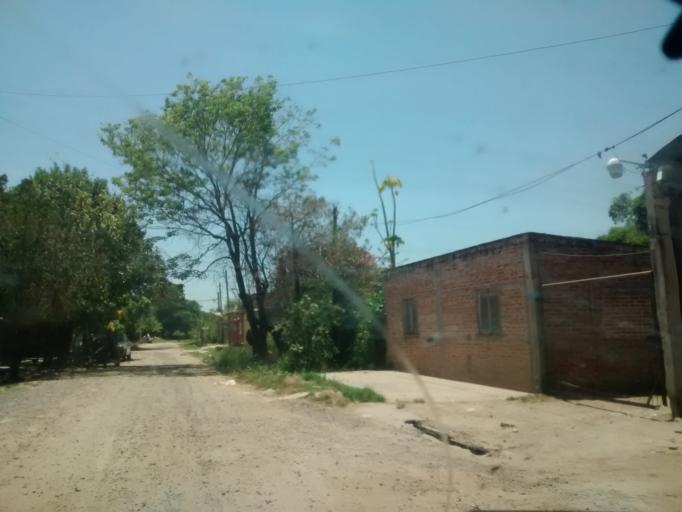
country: AR
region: Chaco
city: Resistencia
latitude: -27.4203
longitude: -58.9796
